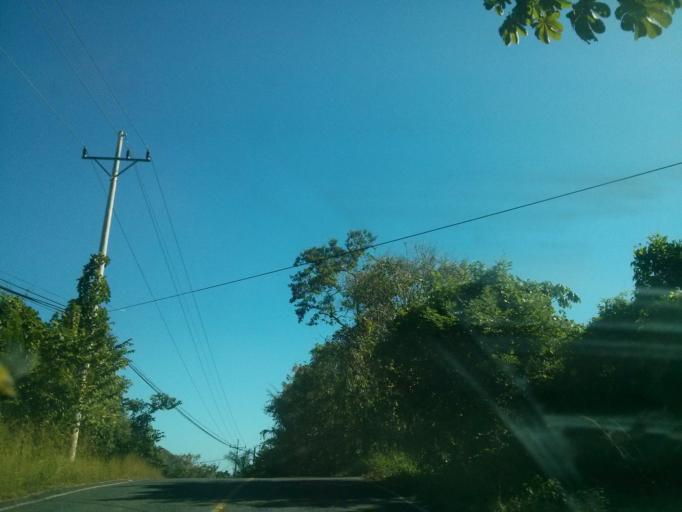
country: CR
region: Puntarenas
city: Paquera
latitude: 9.7034
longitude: -85.0237
